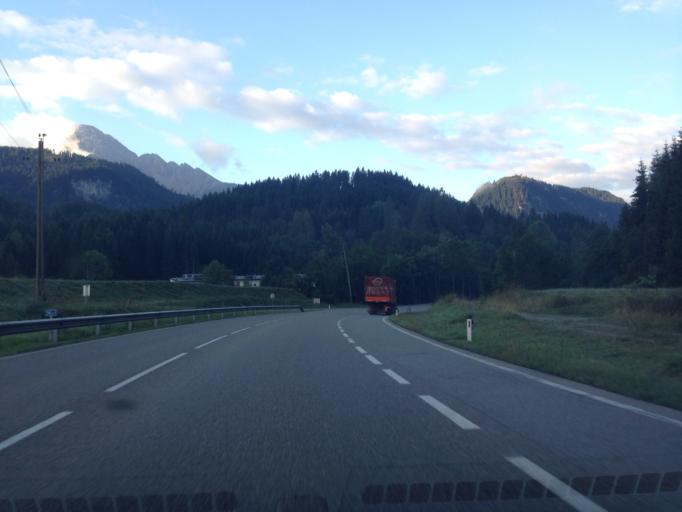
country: AT
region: Tyrol
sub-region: Politischer Bezirk Reutte
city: Breitenwang
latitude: 47.4804
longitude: 10.7349
